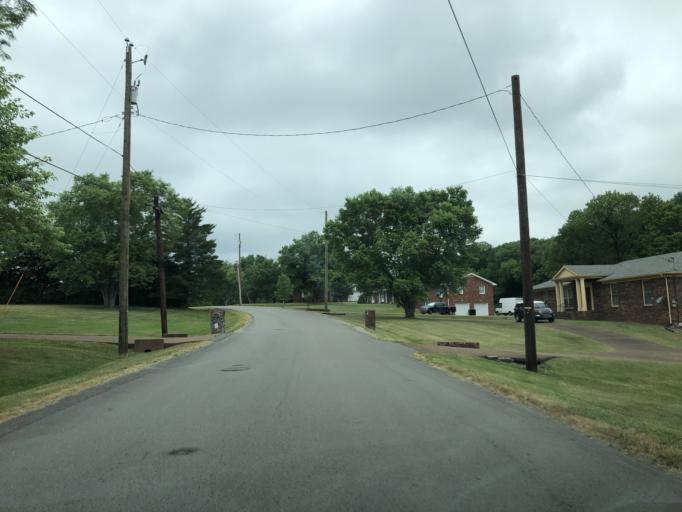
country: US
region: Tennessee
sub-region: Davidson County
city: Goodlettsville
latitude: 36.2796
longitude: -86.7651
